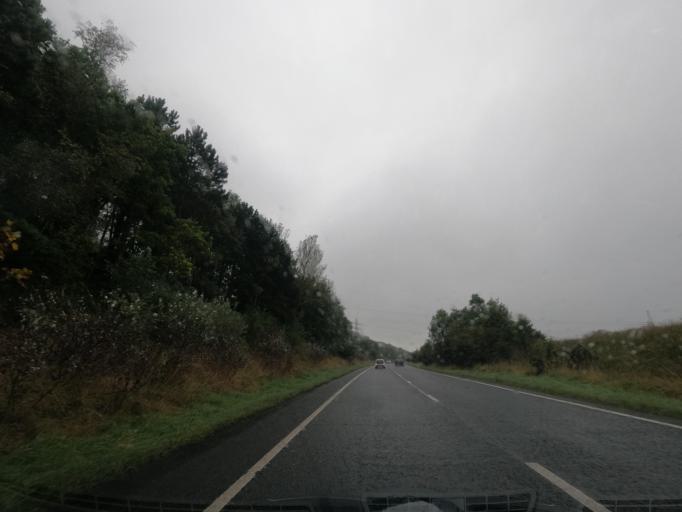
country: GB
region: England
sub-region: Redcar and Cleveland
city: South Bank
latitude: 54.5639
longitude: -1.1236
